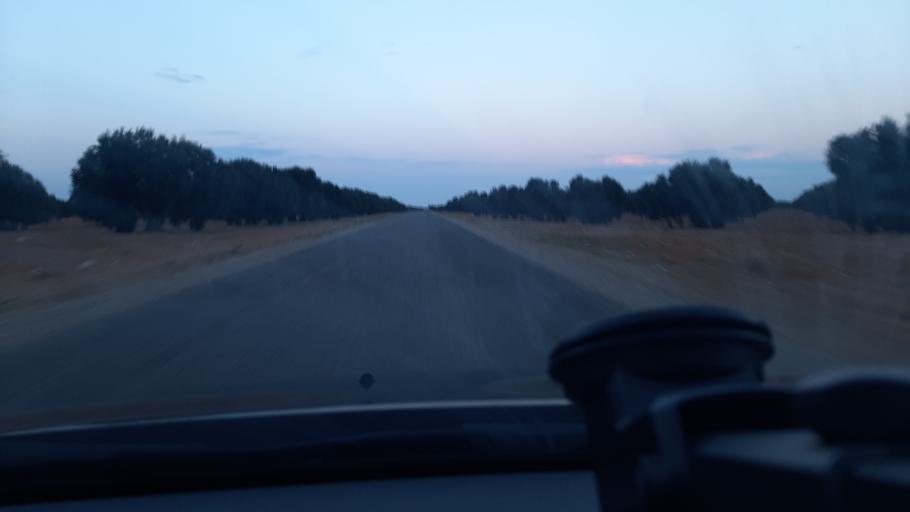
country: TN
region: Al Mahdiyah
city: Shurban
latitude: 34.9974
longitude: 10.4072
